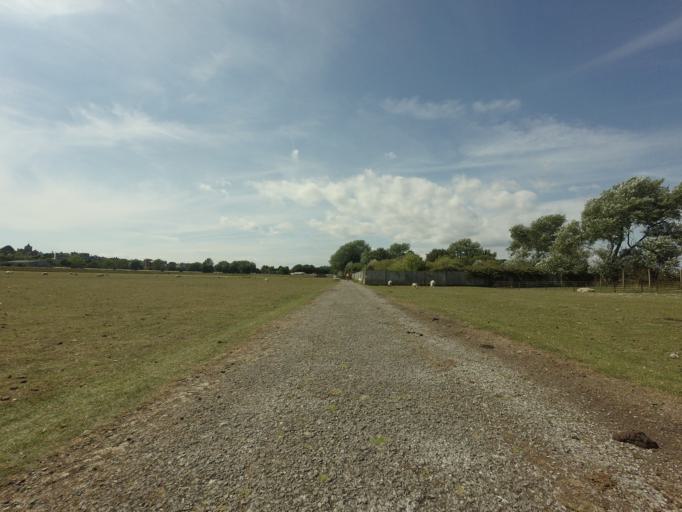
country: GB
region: England
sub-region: East Sussex
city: Rye
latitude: 50.9516
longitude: 0.7434
